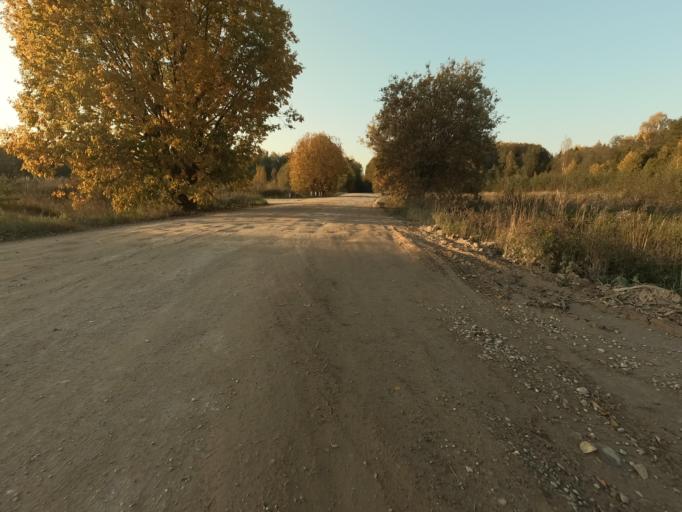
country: RU
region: Leningrad
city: Lyuban'
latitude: 59.0105
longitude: 31.0904
